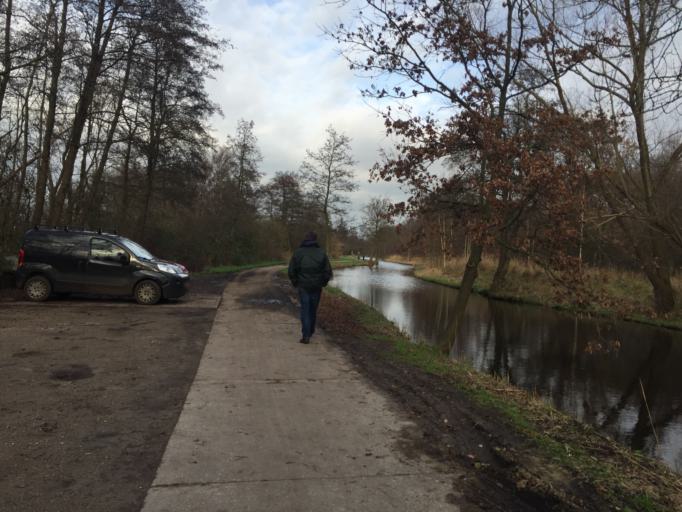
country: NL
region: North Holland
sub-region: Gemeente Wijdemeren
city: Kortenhoef
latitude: 52.2655
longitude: 5.0682
